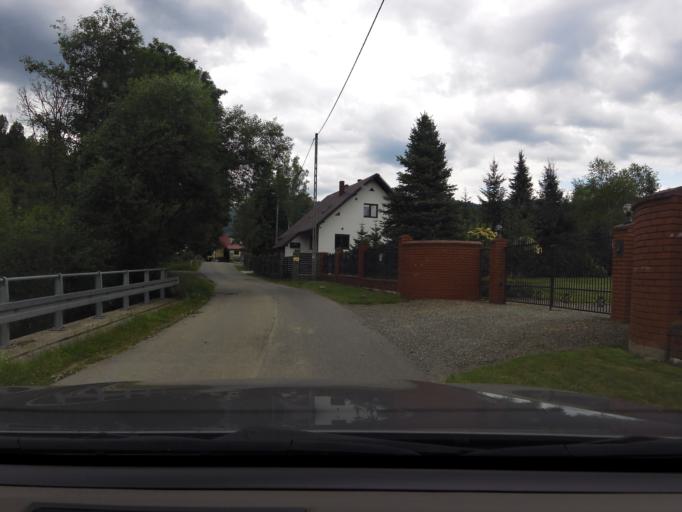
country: PL
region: Silesian Voivodeship
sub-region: Powiat zywiecki
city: Ujsoly
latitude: 49.5030
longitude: 19.1351
